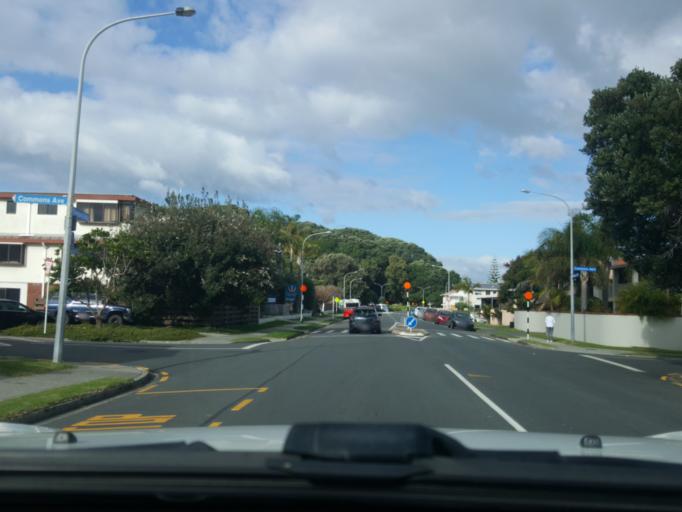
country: NZ
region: Bay of Plenty
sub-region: Tauranga City
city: Tauranga
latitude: -37.6339
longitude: 176.1797
